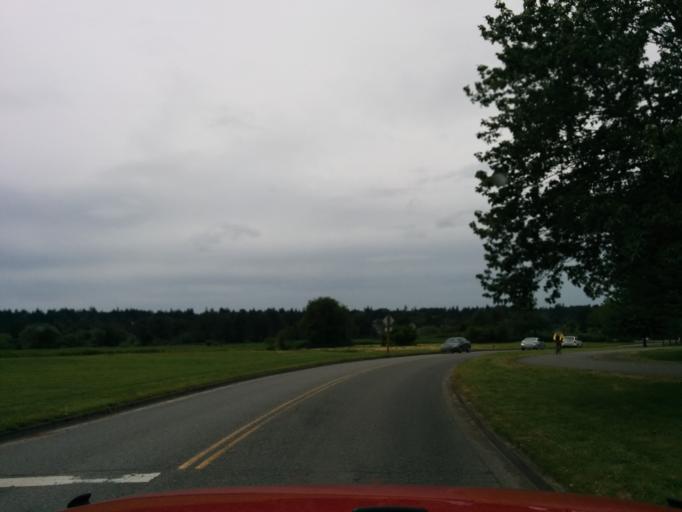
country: US
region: Washington
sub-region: King County
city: Redmond
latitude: 47.6610
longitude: -122.1068
